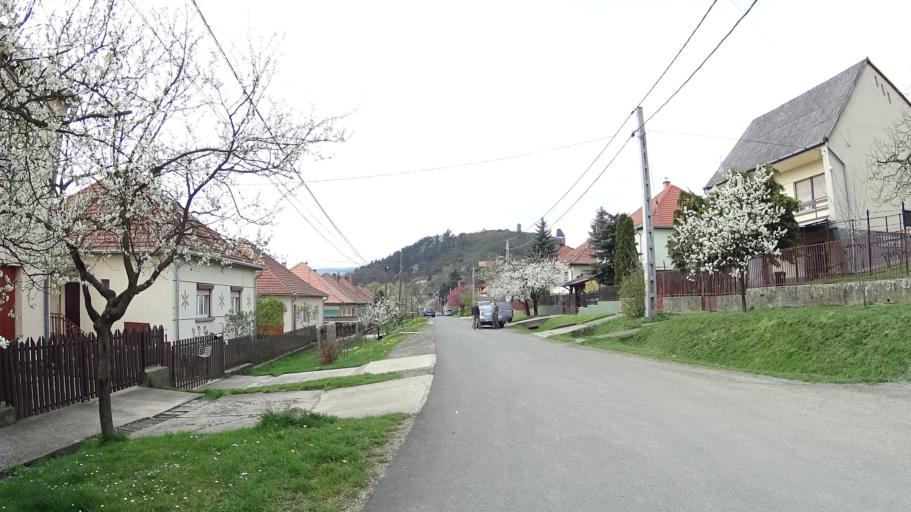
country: HU
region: Nograd
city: Diosjeno
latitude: 47.9037
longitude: 19.0514
